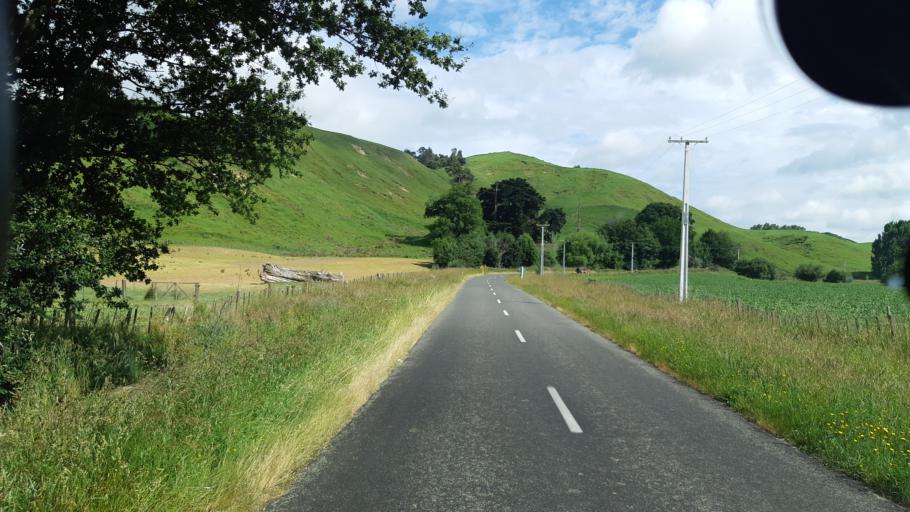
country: NZ
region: Manawatu-Wanganui
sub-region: Rangitikei District
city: Bulls
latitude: -39.9646
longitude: 175.5240
